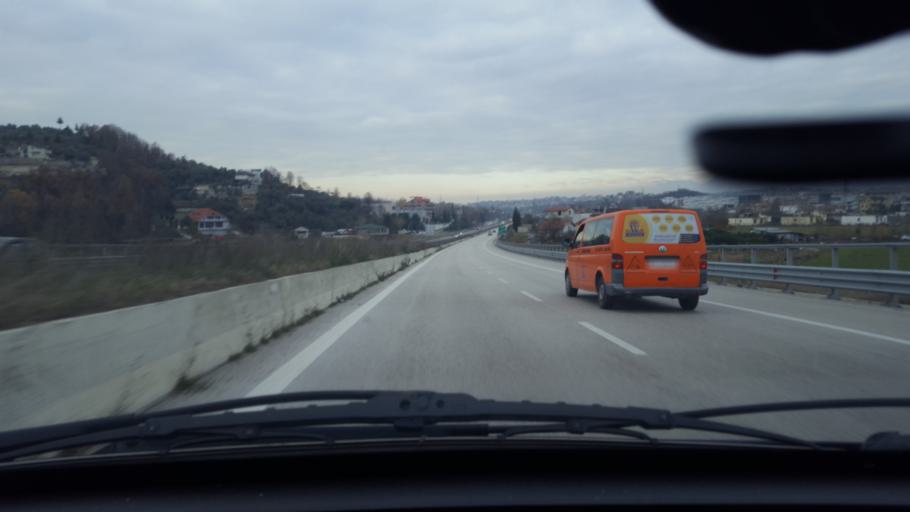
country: AL
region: Tirane
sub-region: Rrethi i Tiranes
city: Petrele
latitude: 41.2748
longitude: 19.8574
